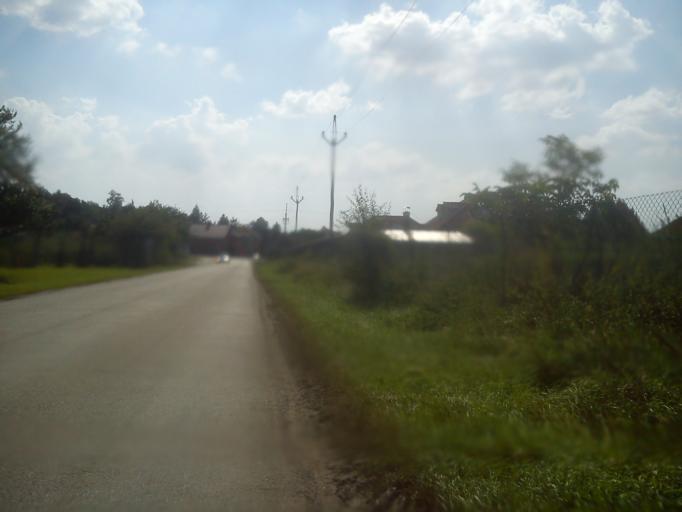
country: CZ
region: South Moravian
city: Sokolnice
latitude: 49.1140
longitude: 16.7283
